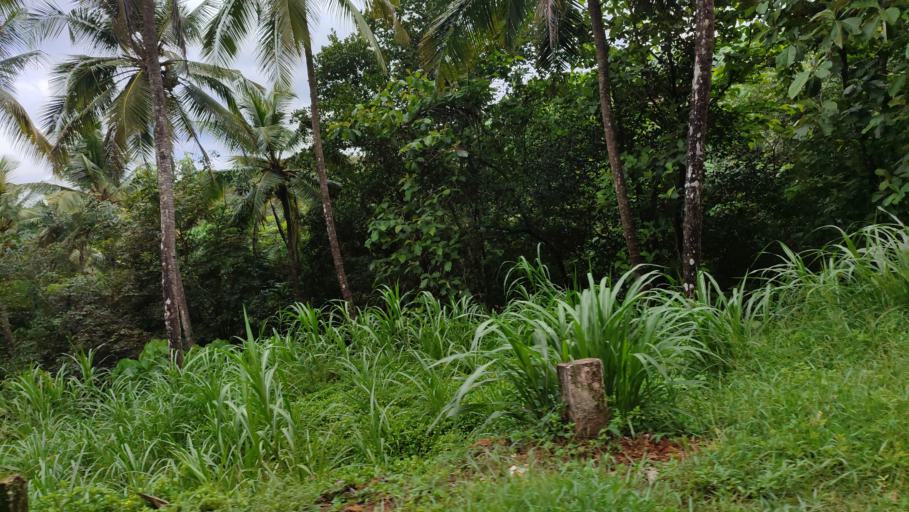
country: IN
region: Kerala
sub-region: Kasaragod District
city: Nileshwar
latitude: 12.2960
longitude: 75.2875
